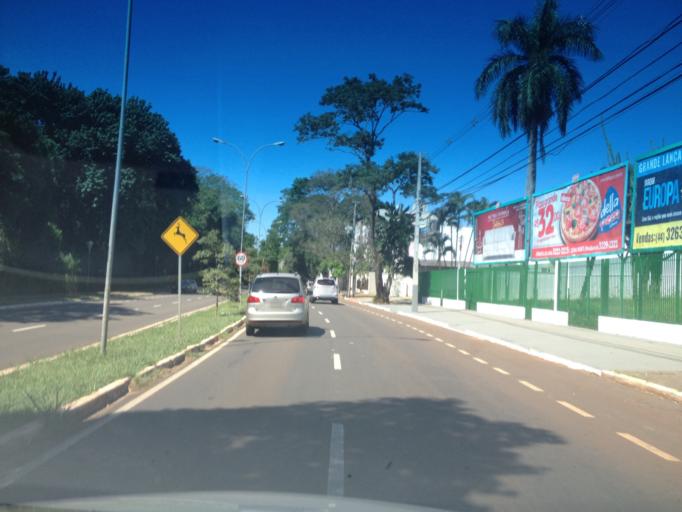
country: BR
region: Parana
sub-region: Maringa
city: Maringa
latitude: -23.4302
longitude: -51.9478
